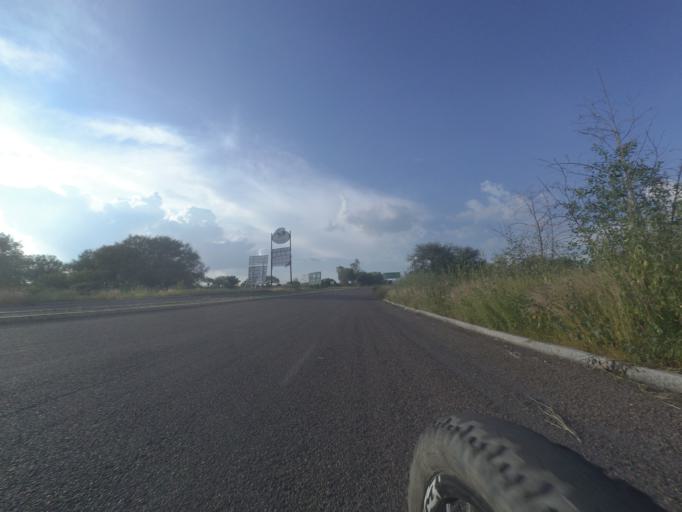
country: MX
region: Aguascalientes
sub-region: Aguascalientes
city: Penuelas (El Cienegal)
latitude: 21.7696
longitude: -102.3586
